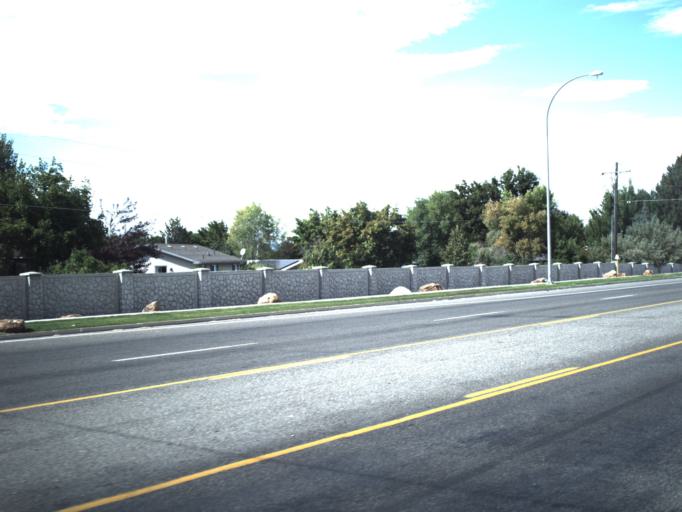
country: US
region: Utah
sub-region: Cache County
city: Smithfield
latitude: 41.8474
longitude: -111.8322
